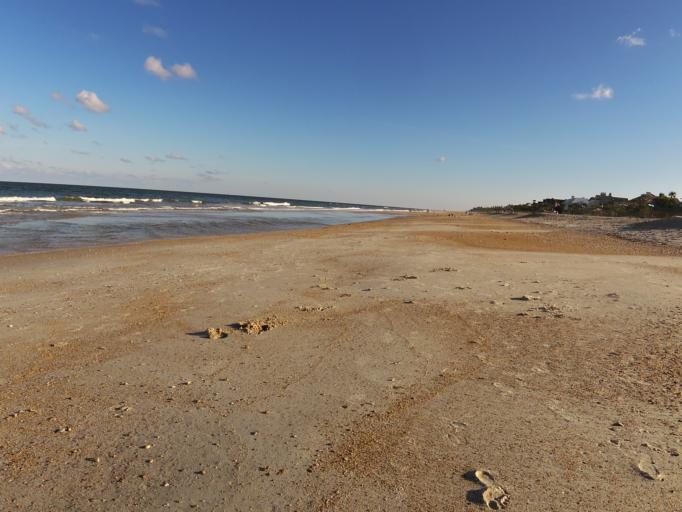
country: US
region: Florida
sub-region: Saint Johns County
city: Sawgrass
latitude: 30.1941
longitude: -81.3641
